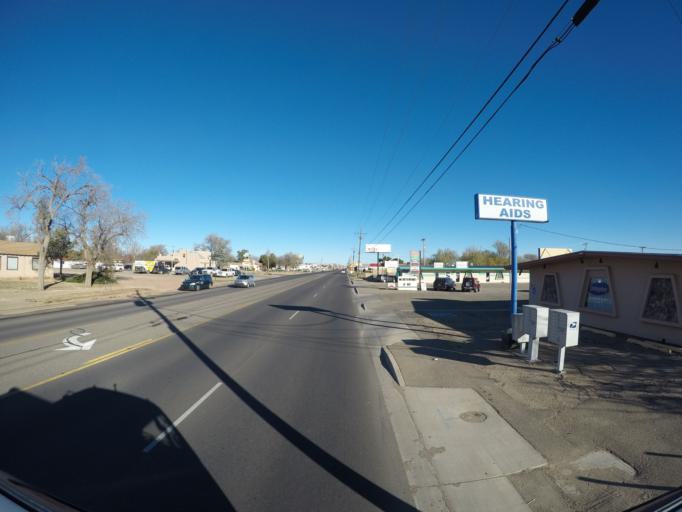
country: US
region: New Mexico
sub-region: Curry County
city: Clovis
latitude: 34.4277
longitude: -103.1964
